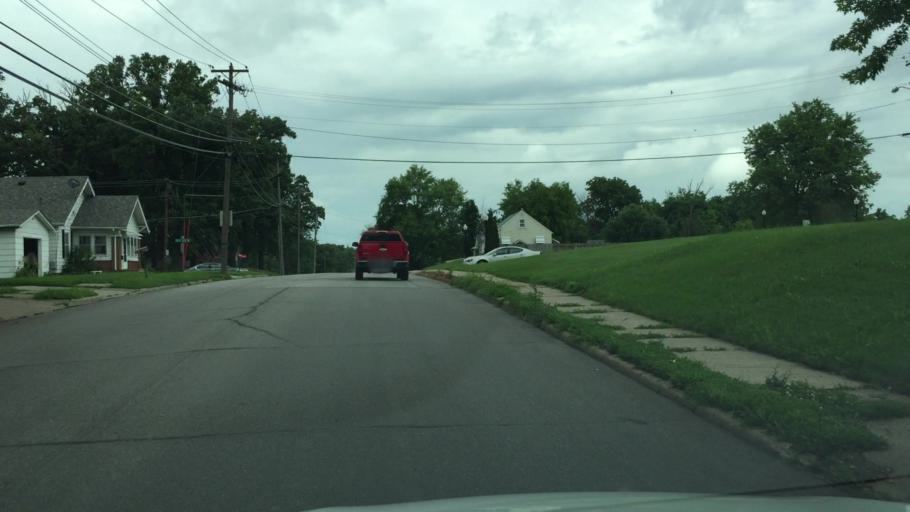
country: US
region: Iowa
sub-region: Jasper County
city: Newton
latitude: 41.7070
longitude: -93.0532
